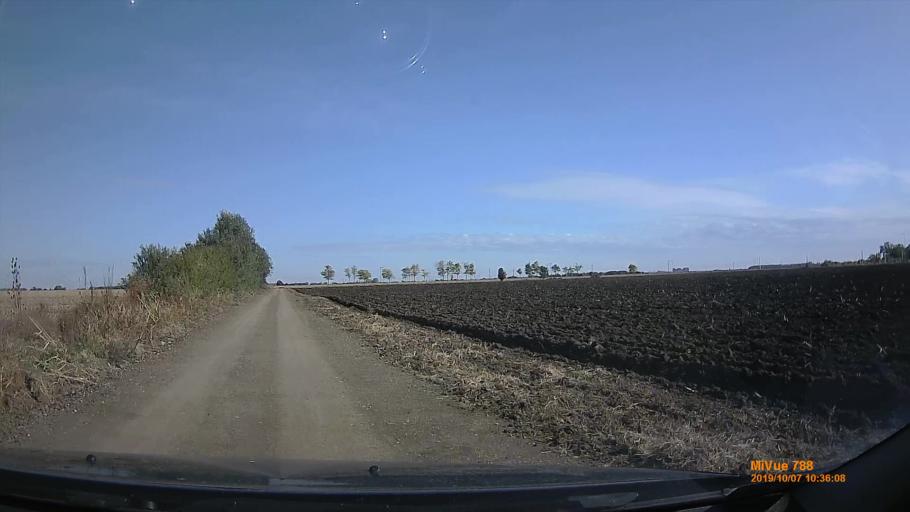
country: HU
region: Bekes
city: Kondoros
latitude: 46.7492
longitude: 20.8485
